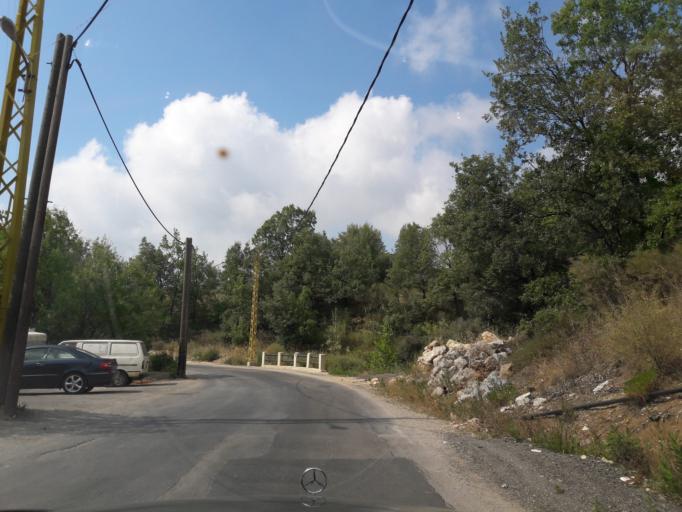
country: LB
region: Mont-Liban
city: Djounie
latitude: 33.9542
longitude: 35.7770
